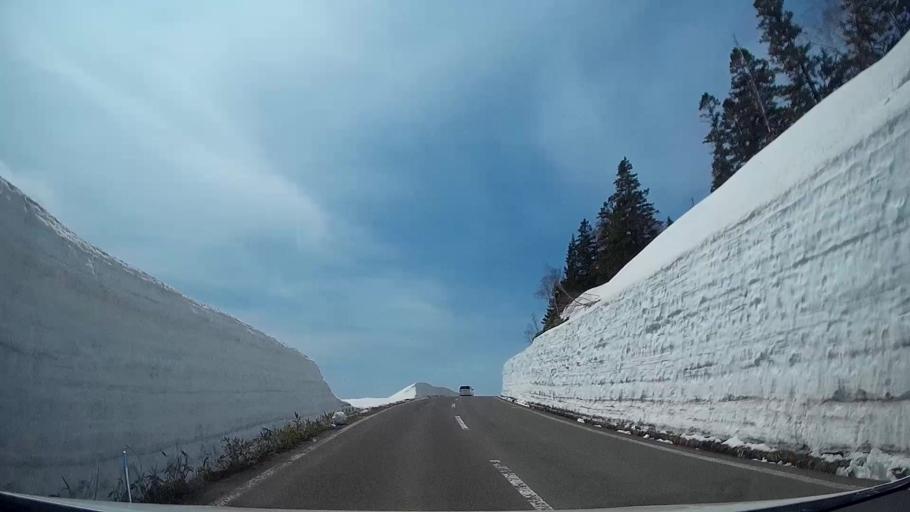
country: JP
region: Akita
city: Hanawa
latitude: 39.9532
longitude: 140.8849
